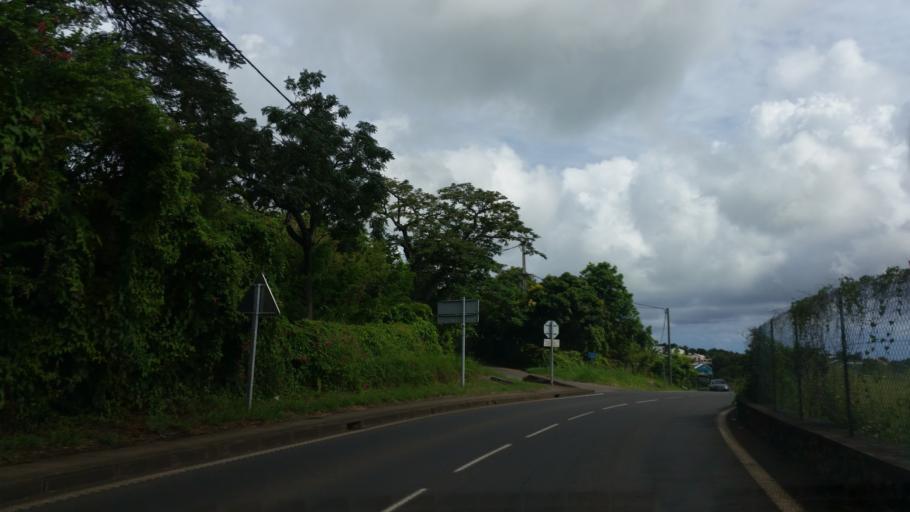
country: RE
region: Reunion
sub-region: Reunion
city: Trois-Bassins
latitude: -21.0674
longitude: 55.2648
